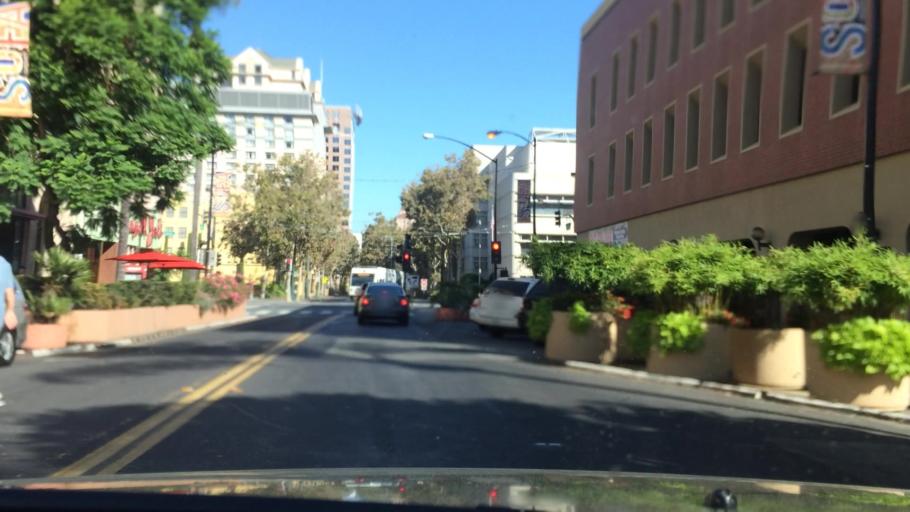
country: US
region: California
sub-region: Santa Clara County
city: San Jose
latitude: 37.3310
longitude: -121.8867
